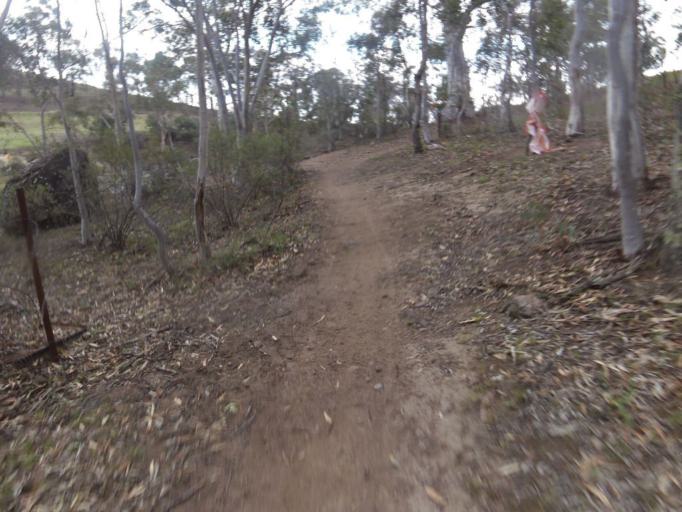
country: AU
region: Australian Capital Territory
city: Forrest
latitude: -35.3483
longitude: 149.1246
